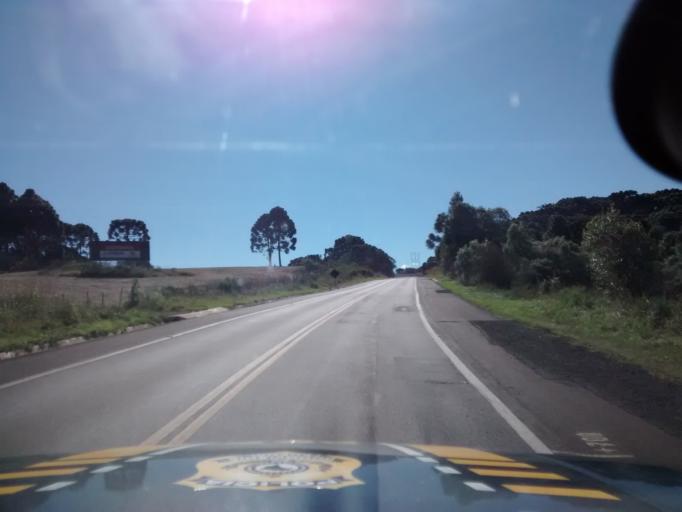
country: BR
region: Rio Grande do Sul
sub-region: Vacaria
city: Vacaria
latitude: -28.3606
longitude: -51.1056
